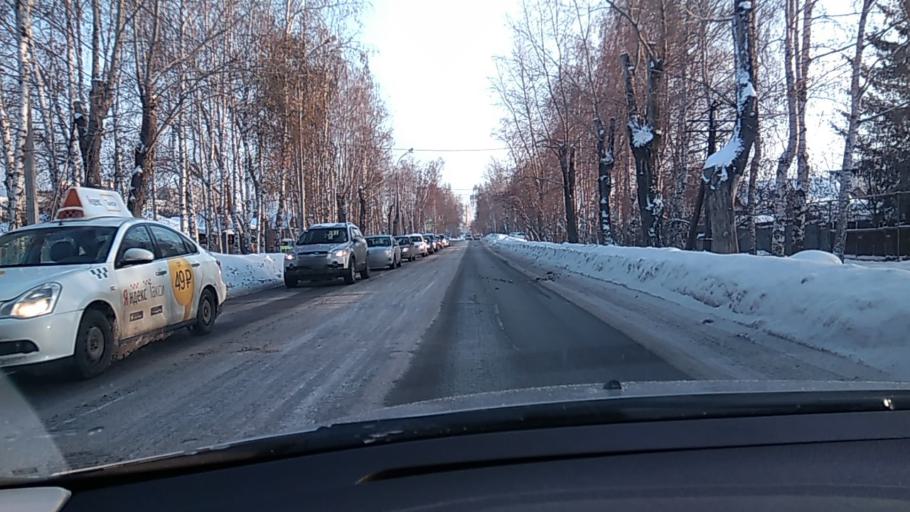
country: RU
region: Sverdlovsk
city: Yekaterinburg
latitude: 56.8086
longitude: 60.5861
